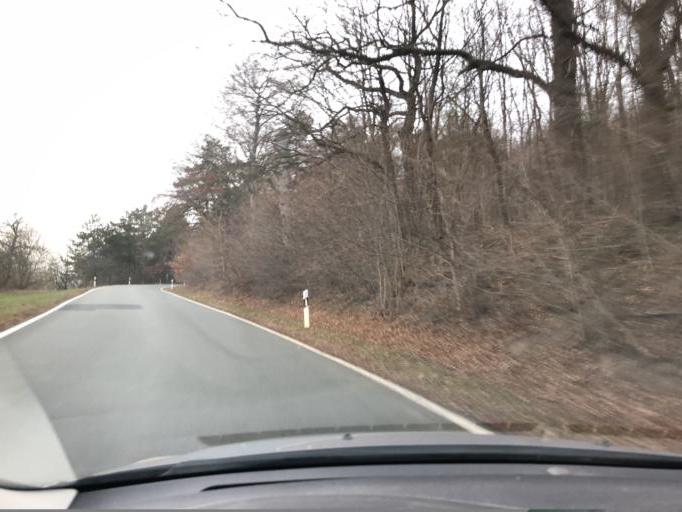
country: DE
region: Saxony-Anhalt
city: Bad Bibra
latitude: 51.1711
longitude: 11.6154
